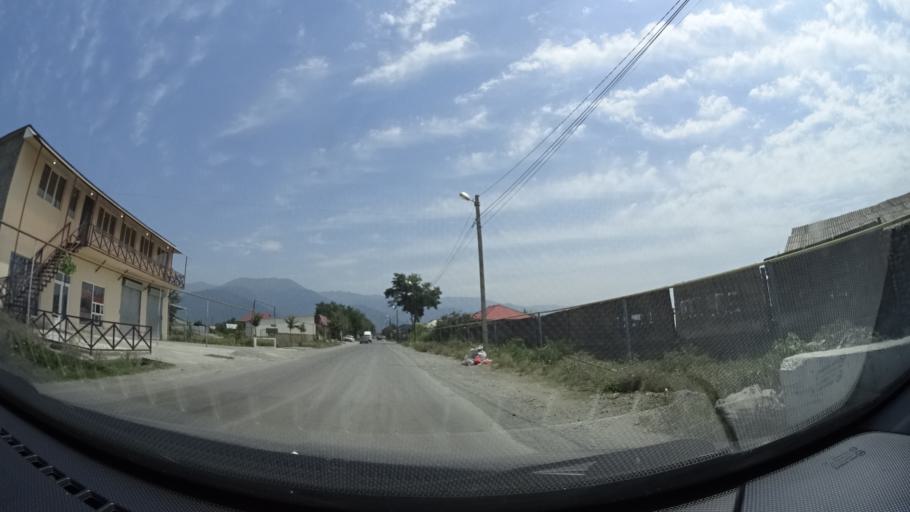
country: GE
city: Bagdadi
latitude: 41.8405
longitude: 46.1126
